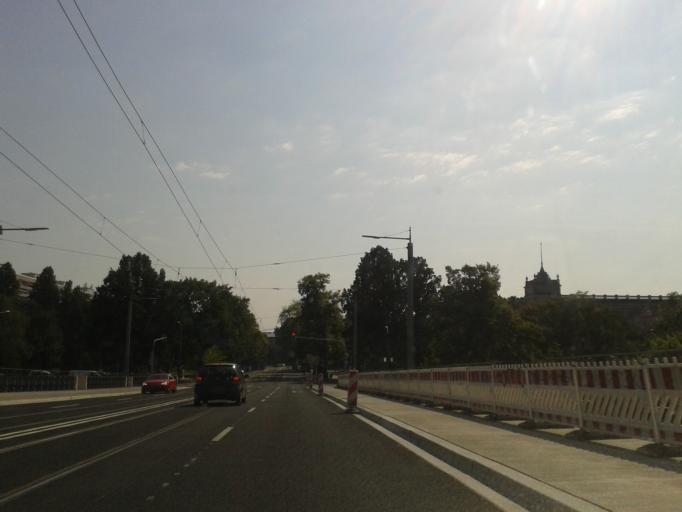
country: DE
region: Saxony
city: Dresden
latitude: 51.0568
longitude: 13.7552
